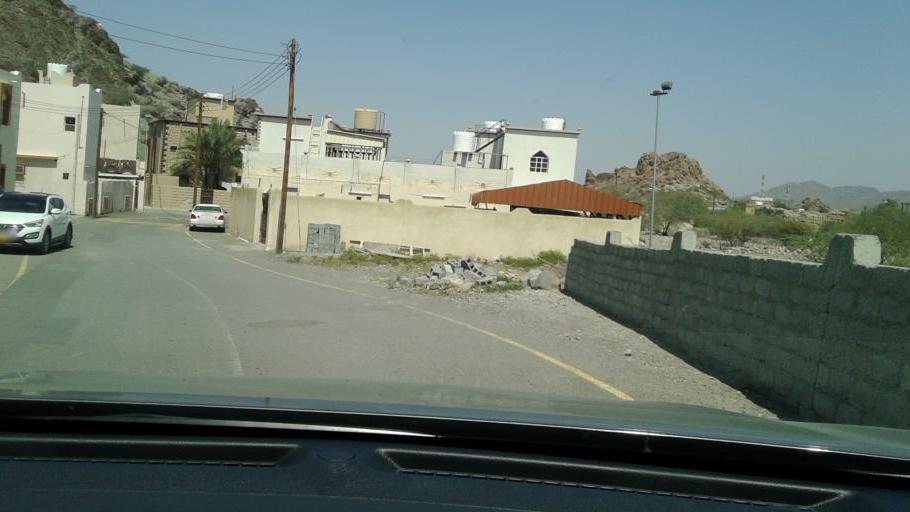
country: OM
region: Al Batinah
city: Rustaq
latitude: 23.3920
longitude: 57.4105
